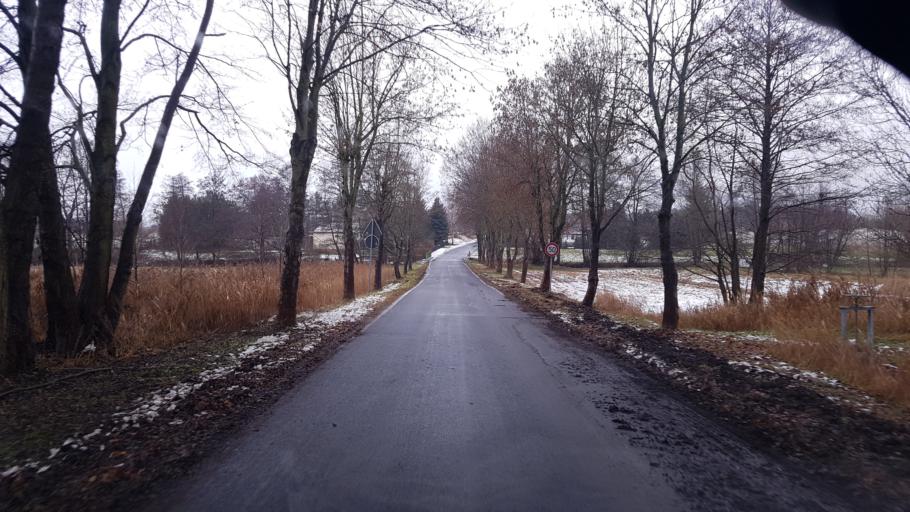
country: DE
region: Brandenburg
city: Jamlitz
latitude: 51.9834
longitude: 14.3391
